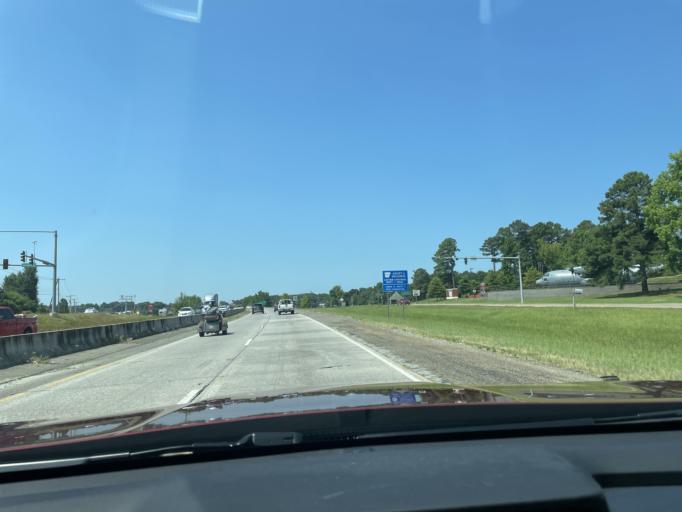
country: US
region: Arkansas
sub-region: Pulaski County
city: Jacksonville
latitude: 34.8897
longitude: -92.1044
